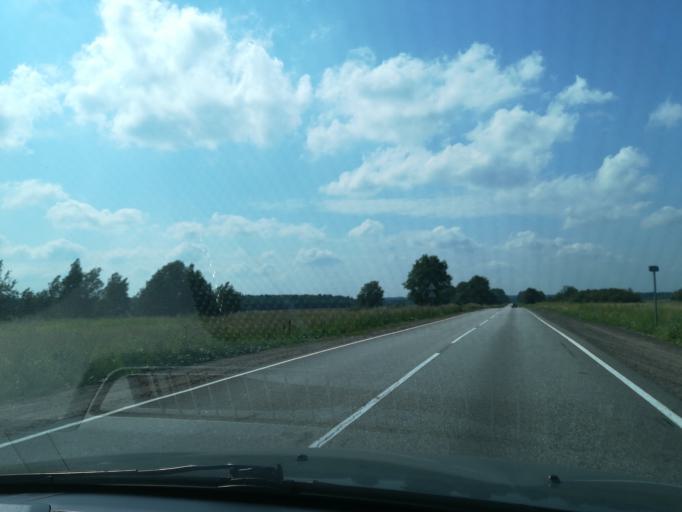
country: RU
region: Leningrad
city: Kopor'ye
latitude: 59.6488
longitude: 29.0080
